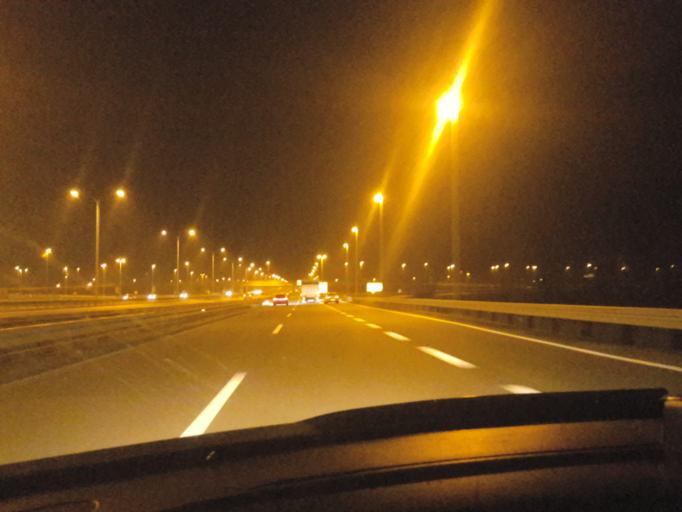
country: RS
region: Autonomna Pokrajina Vojvodina
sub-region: Juznobacki Okrug
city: Novi Sad
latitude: 45.3069
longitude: 19.8358
